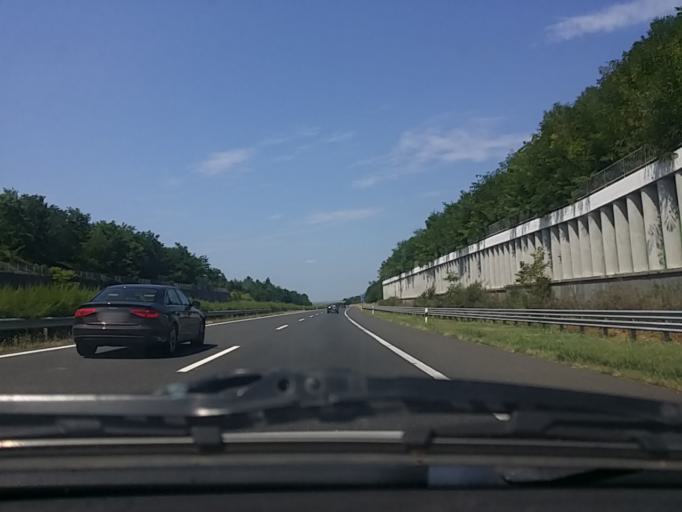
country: HU
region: Somogy
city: Balatonszarszo
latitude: 46.7903
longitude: 17.7767
